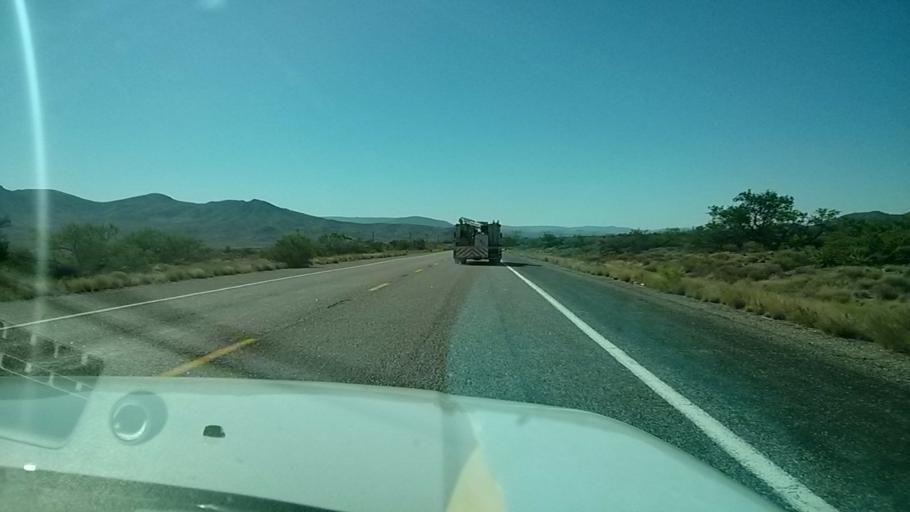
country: US
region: Arizona
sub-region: Mohave County
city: New Kingman-Butler
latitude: 35.4056
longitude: -113.7686
